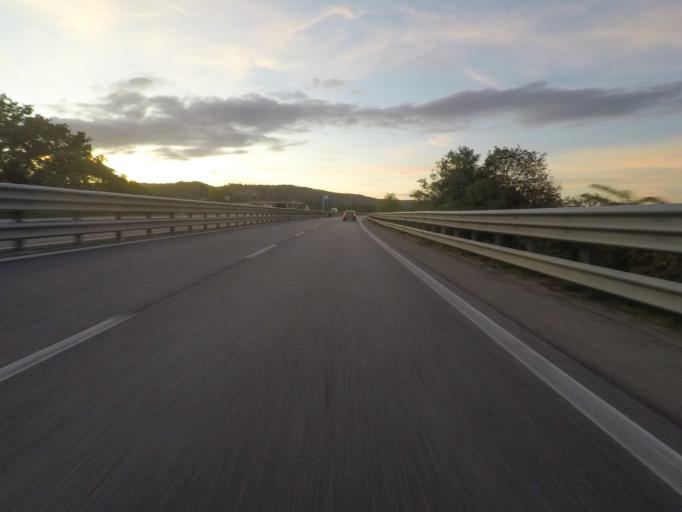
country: IT
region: Tuscany
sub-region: Provincia di Siena
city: Sinalunga
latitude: 43.2268
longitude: 11.7381
